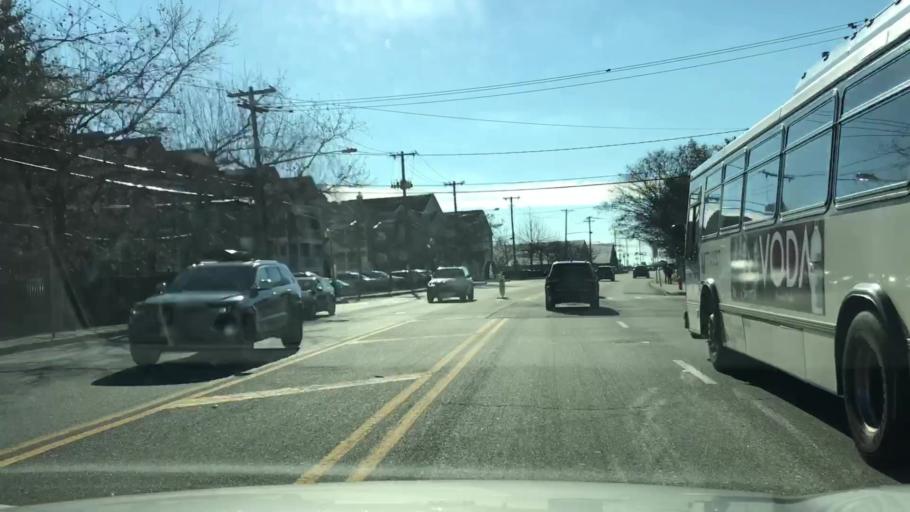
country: US
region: New Jersey
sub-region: Bergen County
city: Edgewater
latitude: 40.8232
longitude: -73.9758
